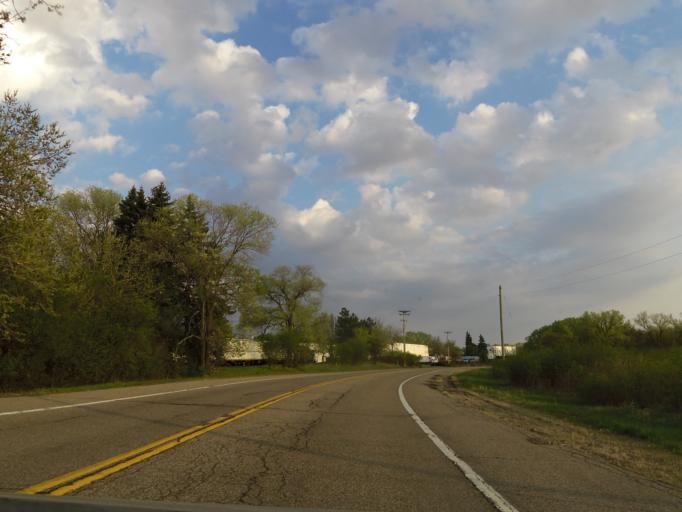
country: US
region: Minnesota
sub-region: Dakota County
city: Mendota Heights
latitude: 44.8720
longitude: -93.1728
